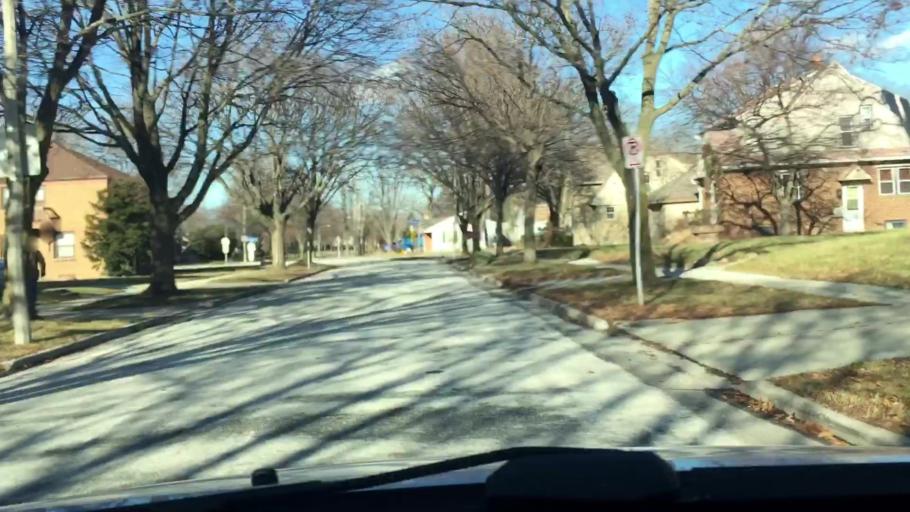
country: US
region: Wisconsin
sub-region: Milwaukee County
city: Wauwatosa
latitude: 43.0351
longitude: -87.9998
